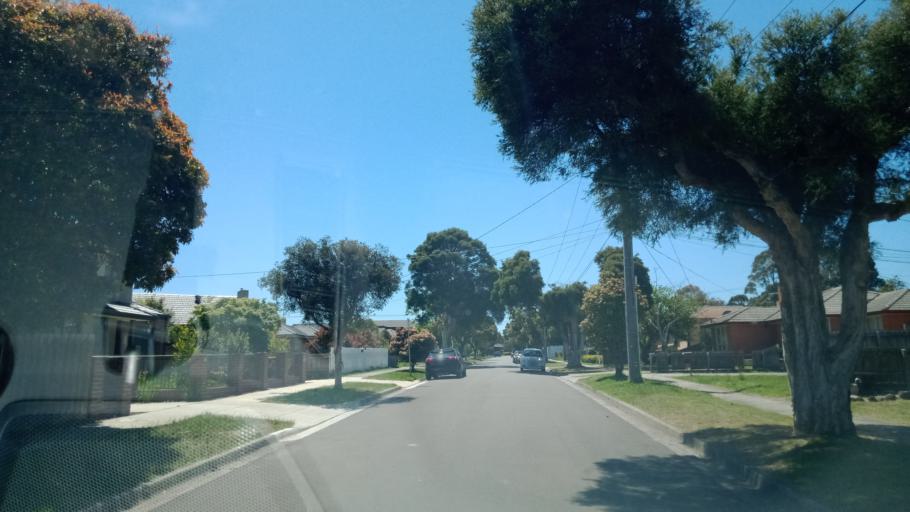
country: AU
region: Victoria
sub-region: Greater Dandenong
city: Springvale
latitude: -37.9300
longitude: 145.1701
